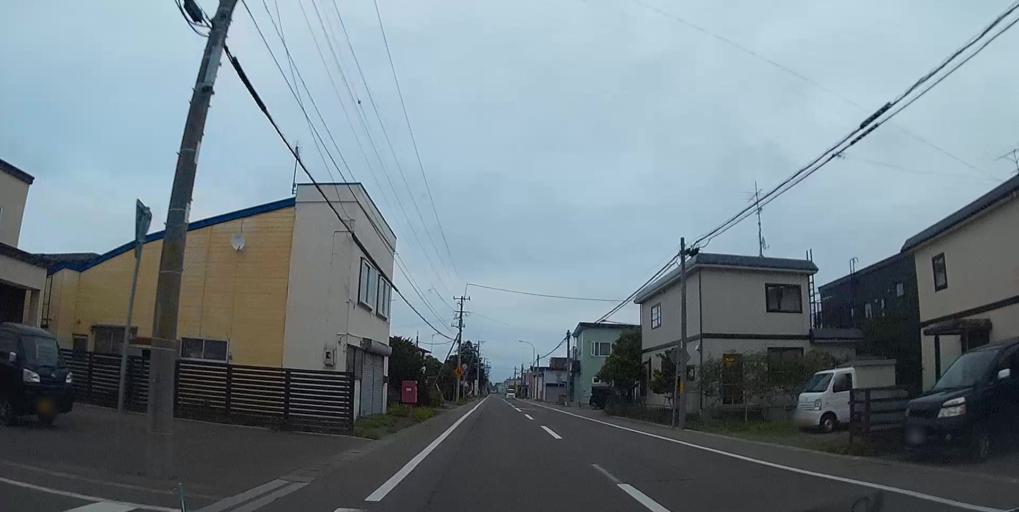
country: JP
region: Hokkaido
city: Nanae
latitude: 42.2543
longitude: 140.2600
